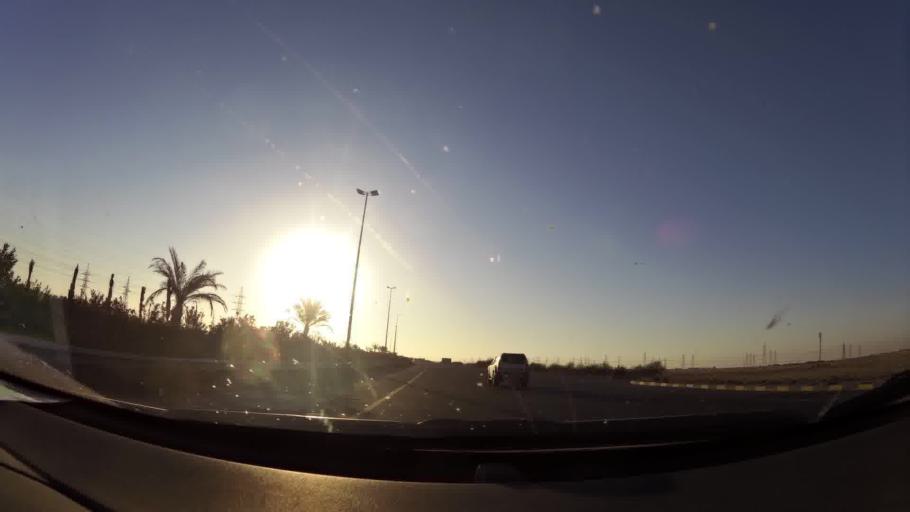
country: KW
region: Al Ahmadi
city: Al Fahahil
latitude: 28.9393
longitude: 48.1853
